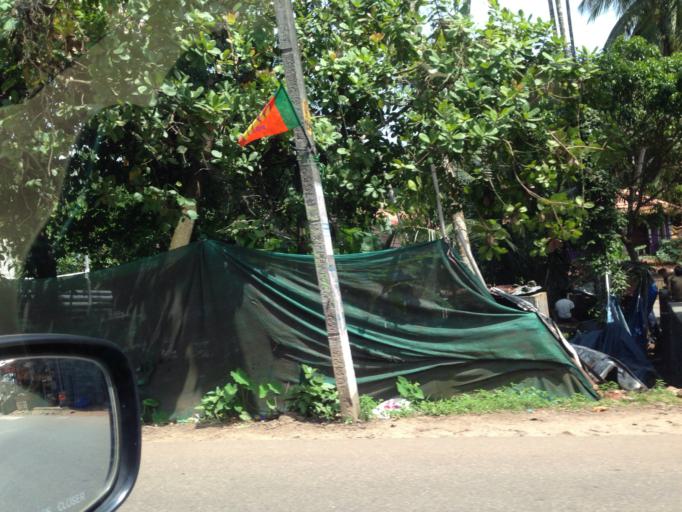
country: IN
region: Kerala
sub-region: Kozhikode
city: Kozhikode
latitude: 11.2868
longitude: 75.7955
